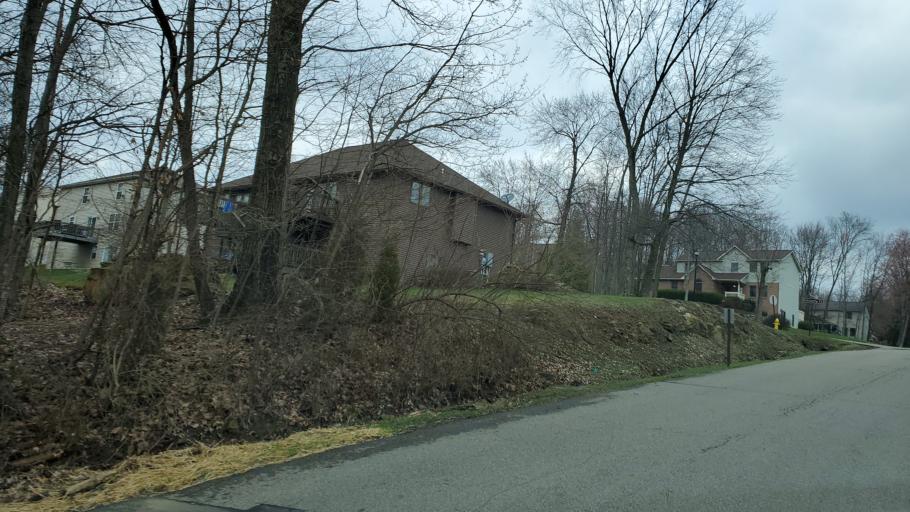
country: US
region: Ohio
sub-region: Licking County
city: Newark
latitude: 40.0322
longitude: -82.3807
